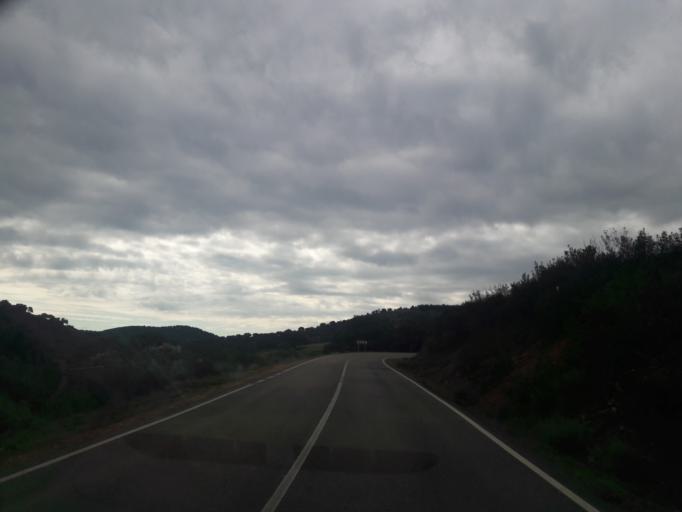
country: ES
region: Castille and Leon
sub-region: Provincia de Salamanca
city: Serradilla del Arroyo
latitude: 40.5243
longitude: -6.4035
